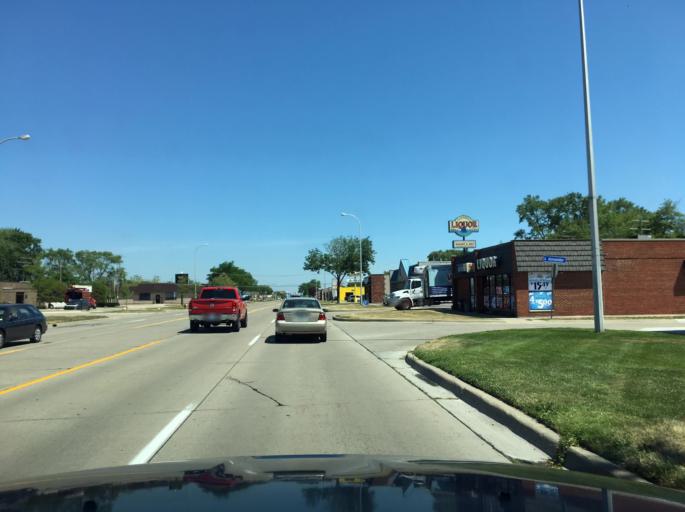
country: US
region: Michigan
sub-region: Macomb County
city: Saint Clair Shores
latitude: 42.4920
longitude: -82.8972
